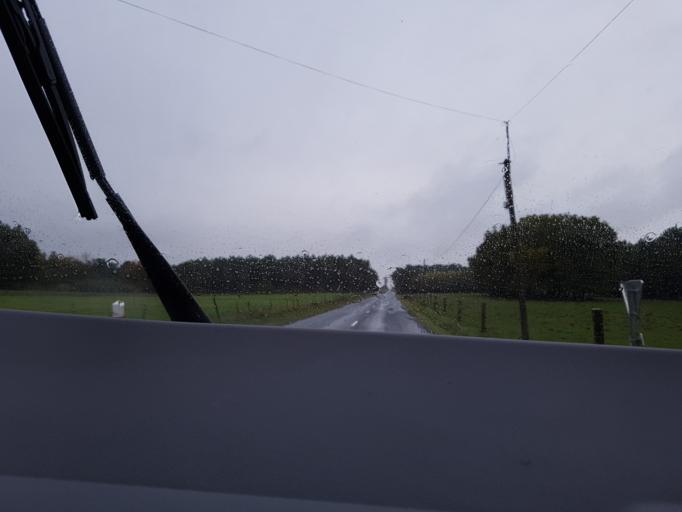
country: FR
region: Aquitaine
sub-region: Departement de la Gironde
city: Reignac
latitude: 45.2245
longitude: -0.5014
